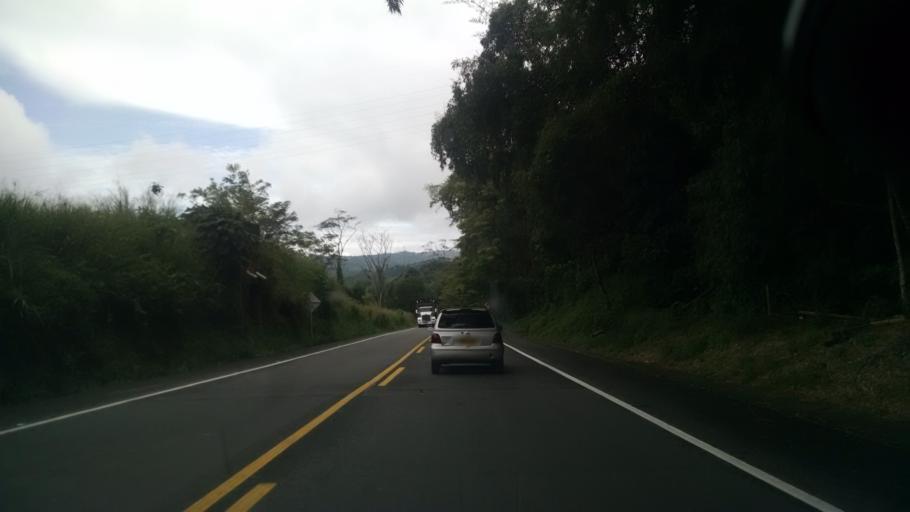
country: CO
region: Caldas
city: Palestina
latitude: 5.0323
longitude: -75.5980
